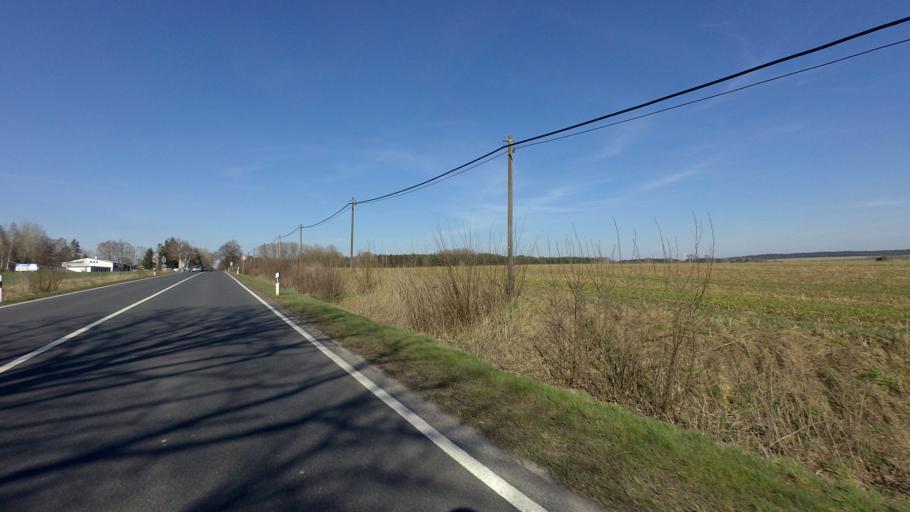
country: DE
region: Brandenburg
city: Angermunde
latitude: 52.9883
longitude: 13.9791
